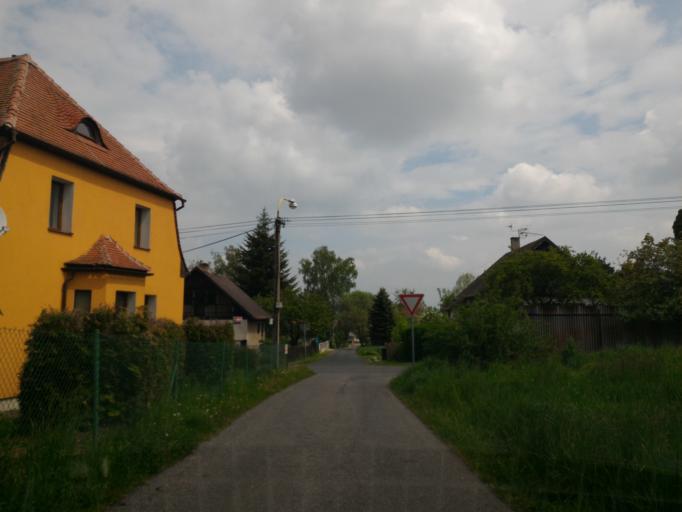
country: CZ
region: Ustecky
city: Varnsdorf
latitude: 50.9009
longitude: 14.6176
